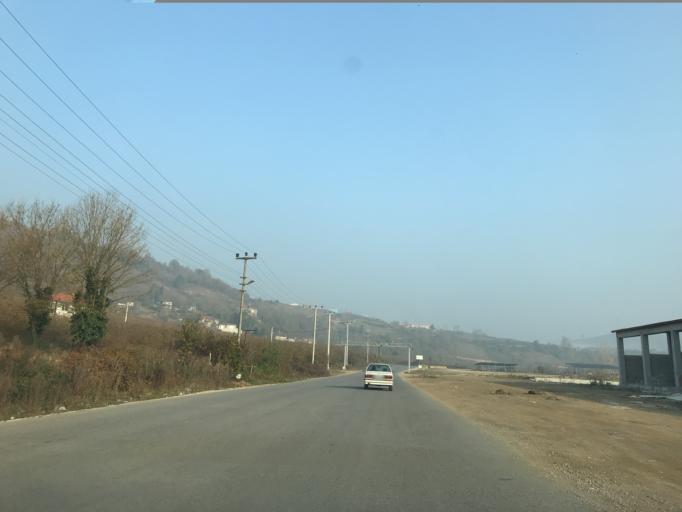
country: TR
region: Duzce
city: Cumayeri
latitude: 40.8853
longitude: 30.9522
